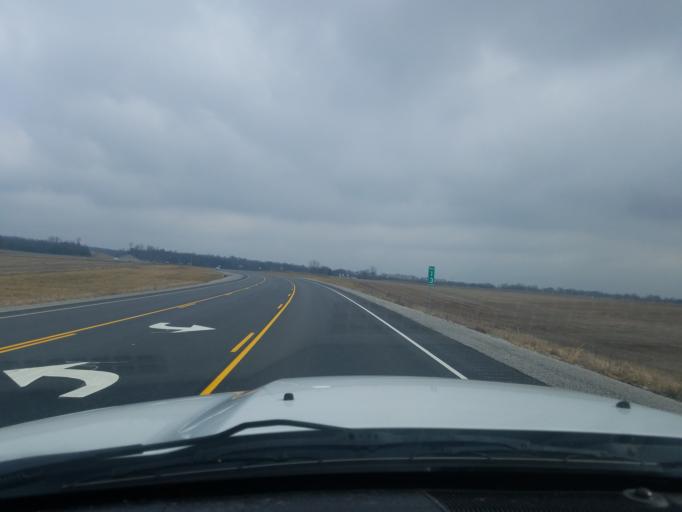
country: US
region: Kentucky
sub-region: Logan County
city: Russellville
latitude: 36.8055
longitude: -86.8846
